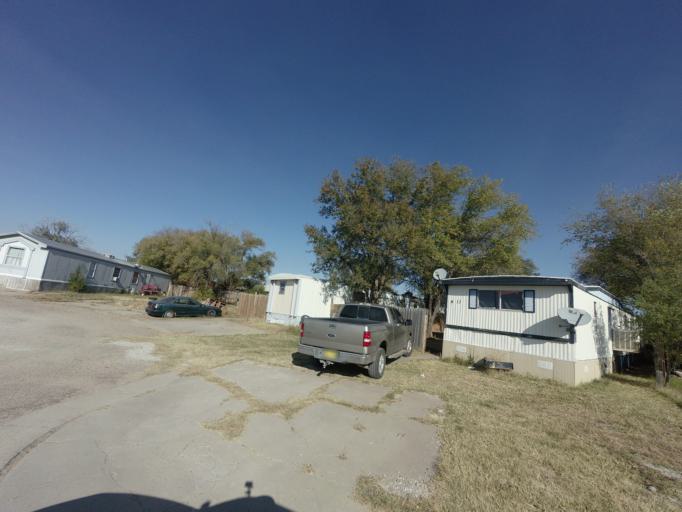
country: US
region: New Mexico
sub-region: Curry County
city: Clovis
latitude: 34.4100
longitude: -103.1748
